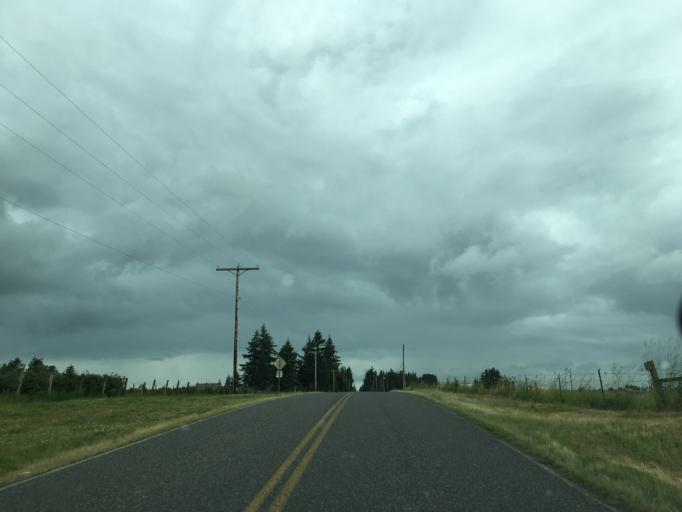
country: US
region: Washington
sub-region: Whatcom County
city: Everson
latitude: 48.9786
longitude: -122.3864
